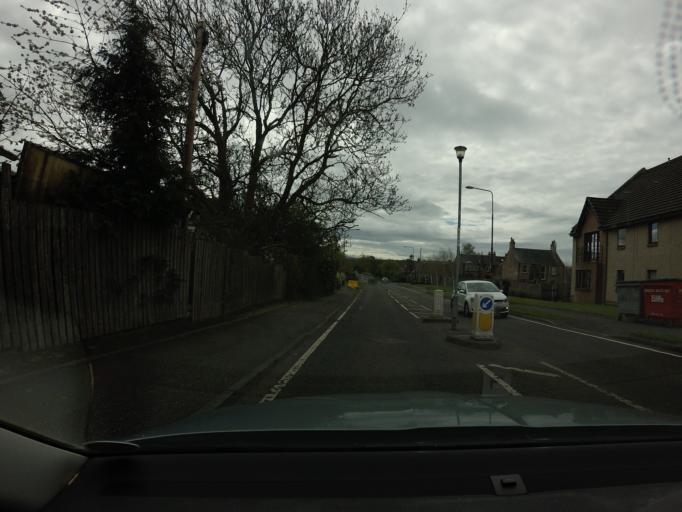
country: GB
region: Scotland
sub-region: West Lothian
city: Broxburn
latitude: 55.9342
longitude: -3.4822
